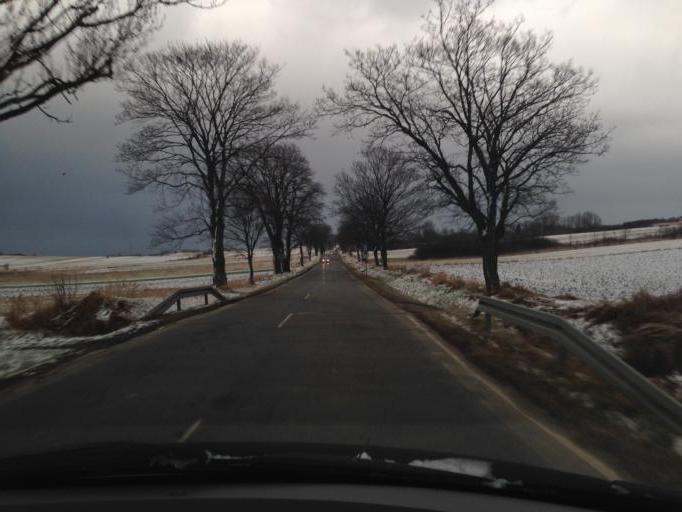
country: PL
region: Subcarpathian Voivodeship
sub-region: Powiat jasielski
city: Osiek Jasielski
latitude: 49.6105
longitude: 21.4916
